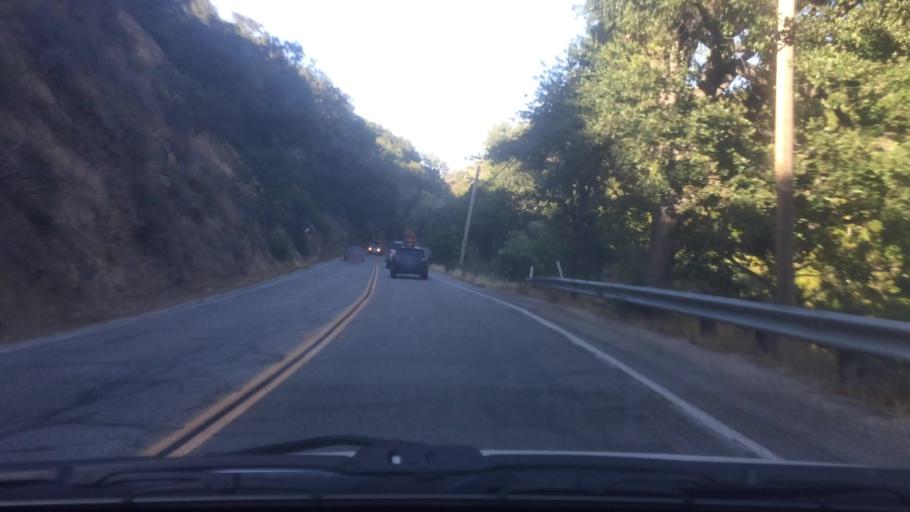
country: US
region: California
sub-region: San Luis Obispo County
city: Atascadero
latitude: 35.4509
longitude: -120.6965
